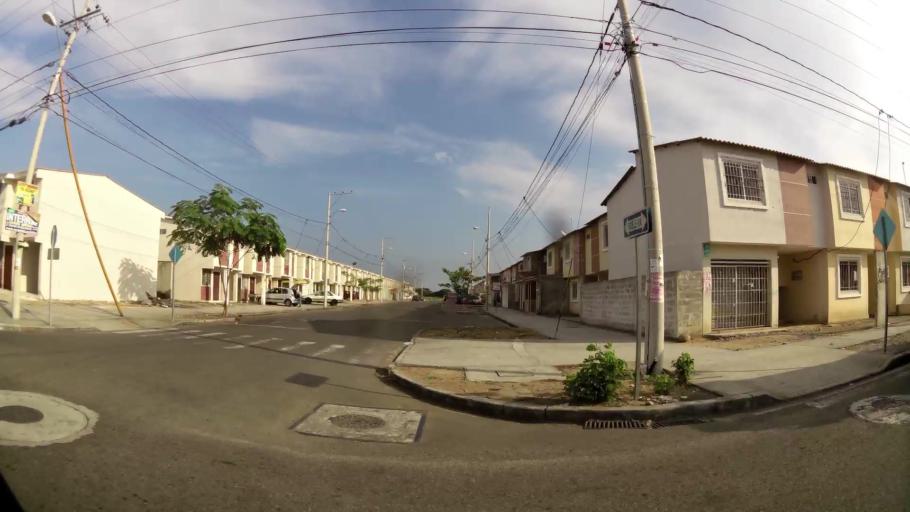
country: EC
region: Guayas
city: Eloy Alfaro
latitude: -2.0616
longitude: -79.8921
